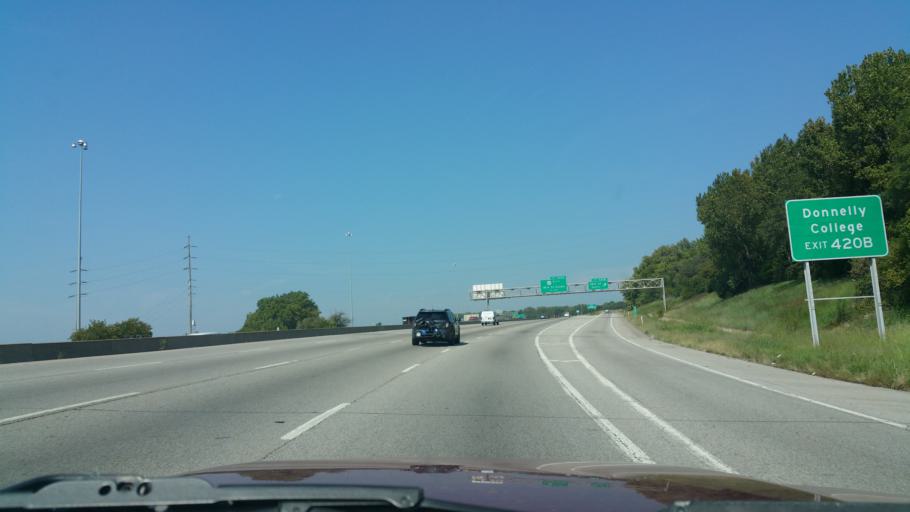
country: US
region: Kansas
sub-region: Wyandotte County
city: Kansas City
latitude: 39.0932
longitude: -94.6427
